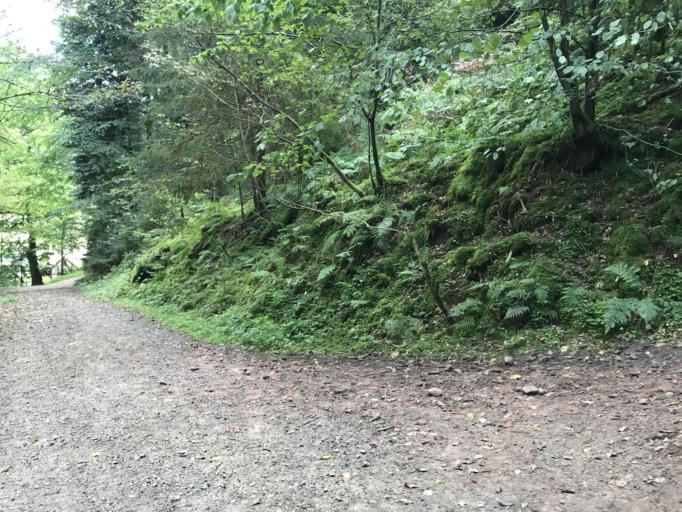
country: DE
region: Baden-Wuerttemberg
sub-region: Karlsruhe Region
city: Calw
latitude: 48.6966
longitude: 8.7269
